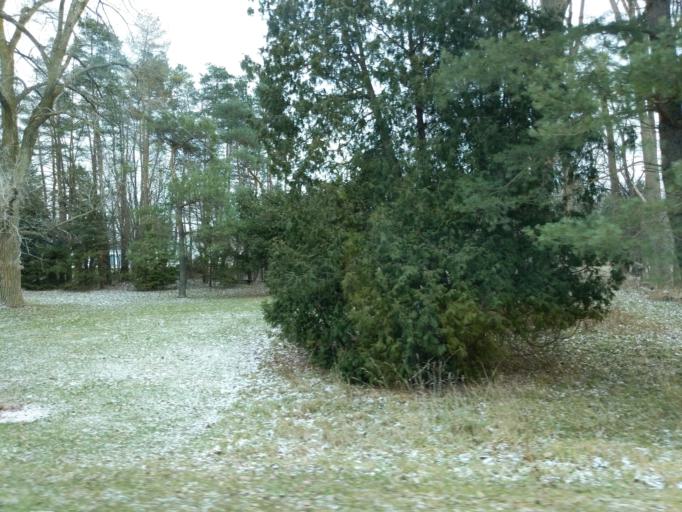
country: US
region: Michigan
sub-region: Lapeer County
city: North Branch
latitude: 43.3116
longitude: -83.1792
